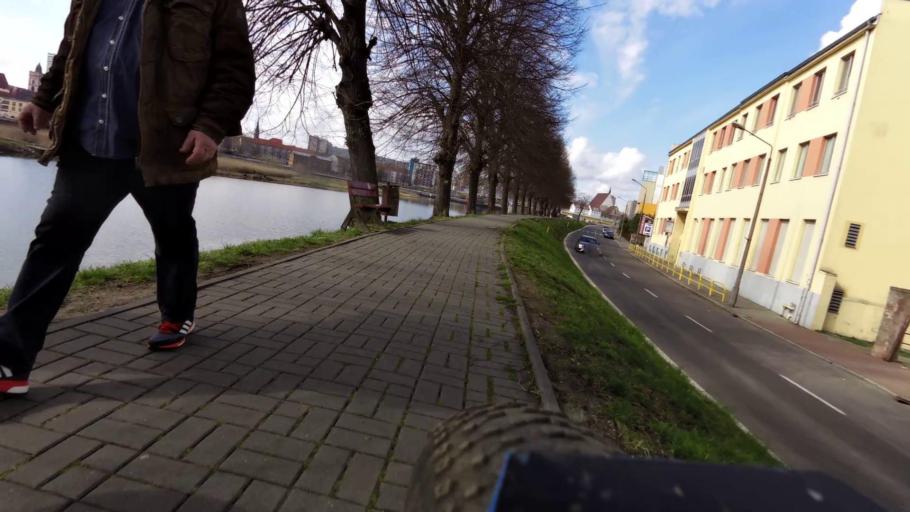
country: PL
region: Lubusz
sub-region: Powiat slubicki
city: Slubice
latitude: 52.3475
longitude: 14.5613
